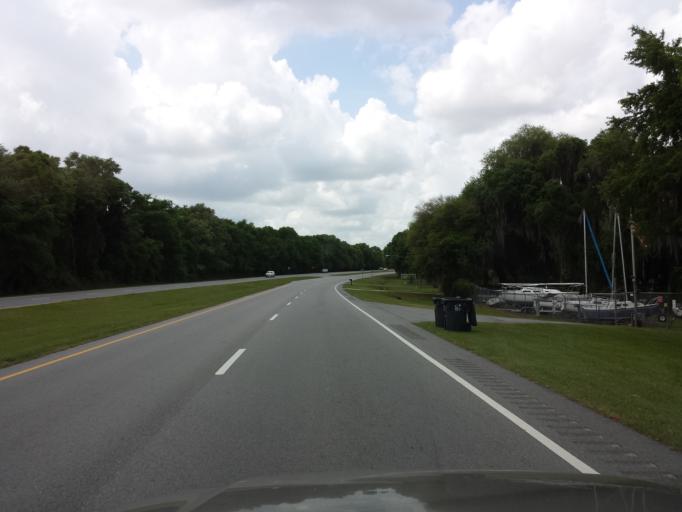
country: US
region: Georgia
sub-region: Lowndes County
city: Valdosta
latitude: 30.6880
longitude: -83.2024
